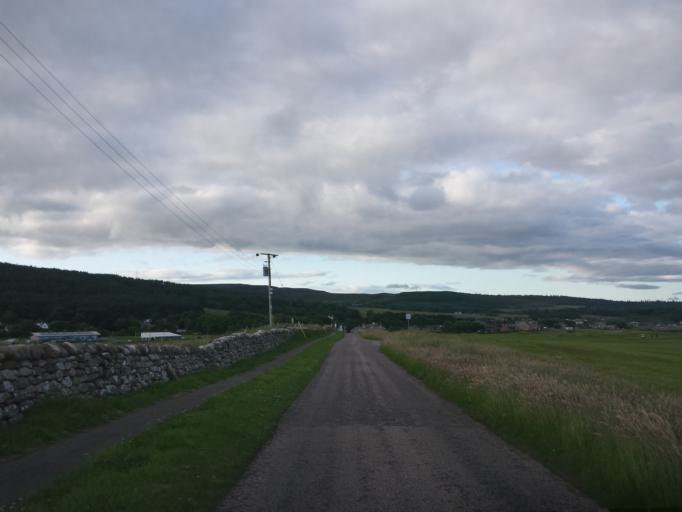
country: GB
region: Scotland
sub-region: Highland
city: Golspie
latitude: 57.9656
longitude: -3.9907
